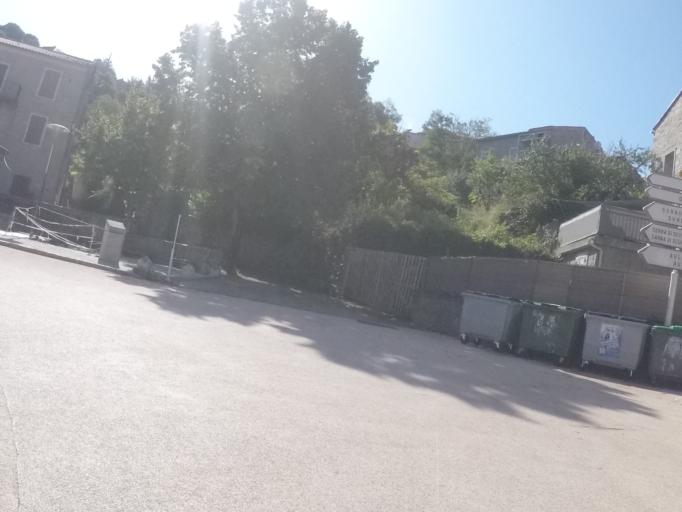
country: FR
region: Corsica
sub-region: Departement de la Corse-du-Sud
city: Albitreccia
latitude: 41.7842
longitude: 8.9795
